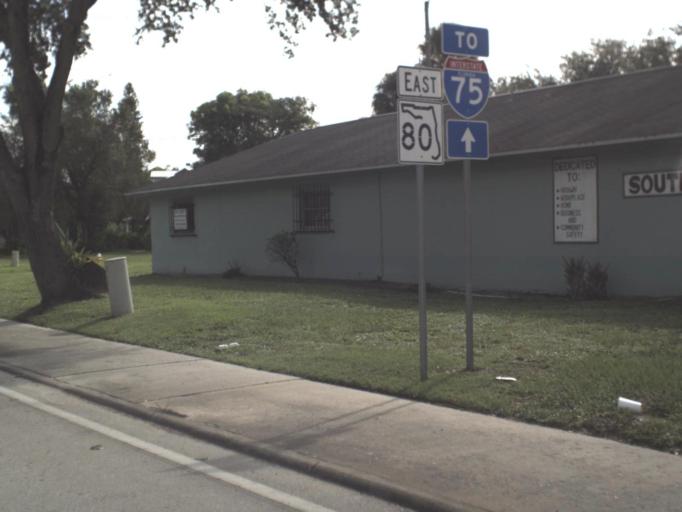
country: US
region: Florida
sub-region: Lee County
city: North Fort Myers
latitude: 26.6468
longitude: -81.8609
